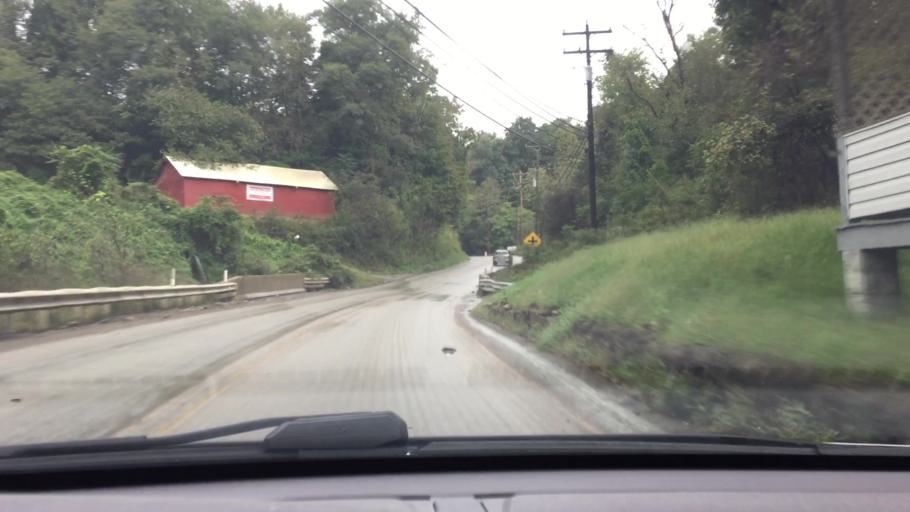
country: US
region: Pennsylvania
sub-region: Westmoreland County
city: Lynnwood-Pricedale
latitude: 40.1427
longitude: -79.8584
